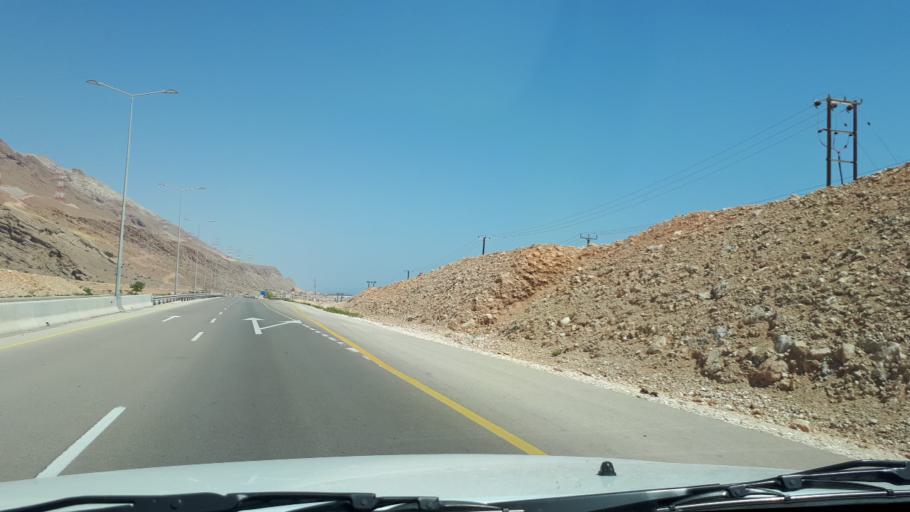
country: OM
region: Ash Sharqiyah
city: Sur
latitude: 22.7838
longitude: 59.2791
